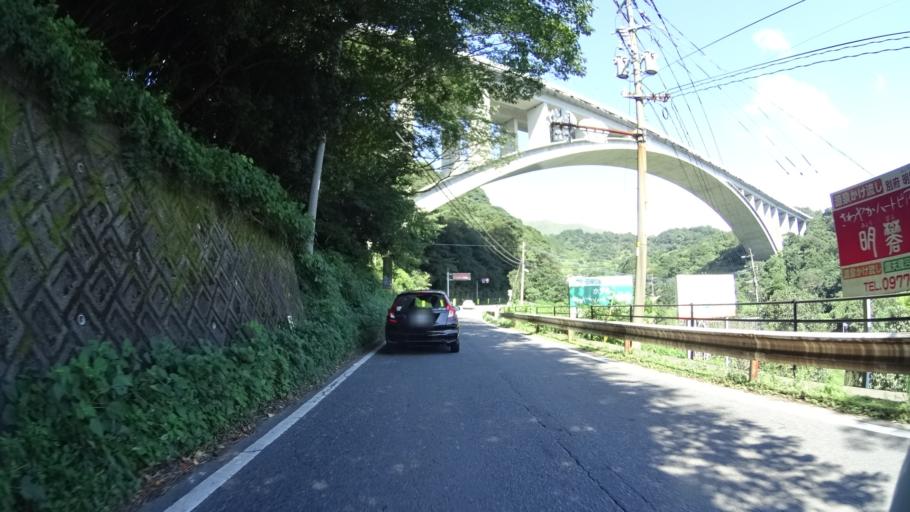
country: JP
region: Oita
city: Beppu
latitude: 33.3148
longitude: 131.4561
